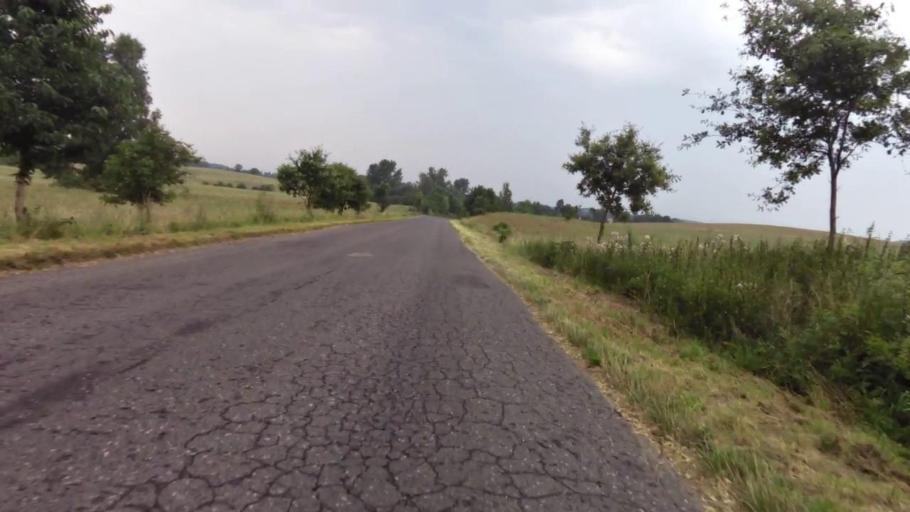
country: PL
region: West Pomeranian Voivodeship
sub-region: Powiat lobeski
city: Wegorzyno
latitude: 53.5032
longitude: 15.6456
